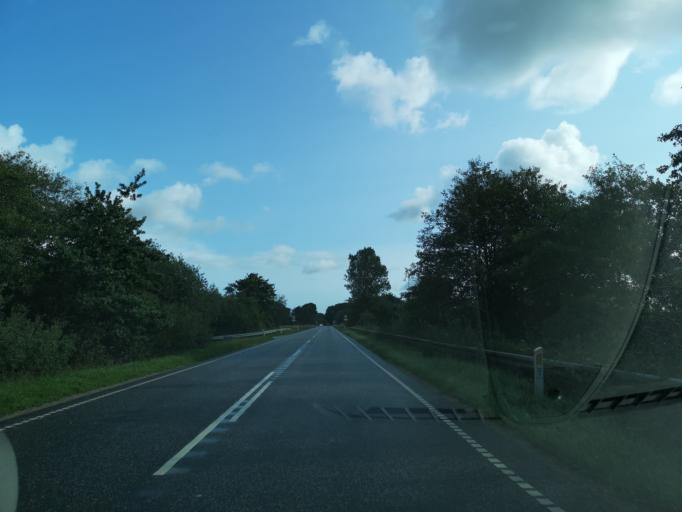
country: DK
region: Central Jutland
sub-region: Ringkobing-Skjern Kommune
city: Videbaek
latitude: 56.0411
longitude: 8.6152
